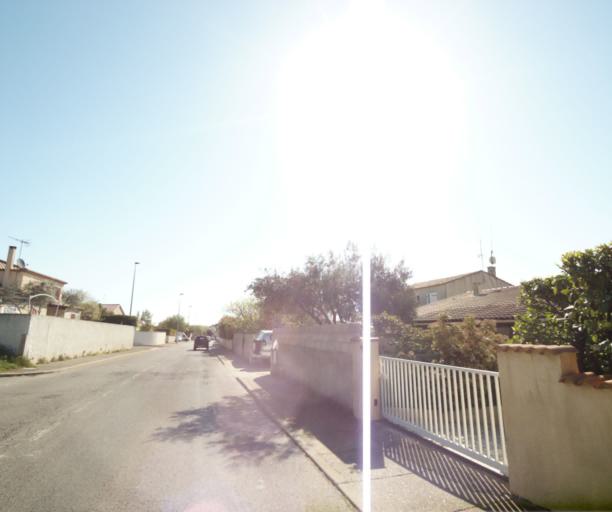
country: FR
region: Languedoc-Roussillon
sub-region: Departement de l'Herault
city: Castelnau-le-Lez
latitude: 43.6365
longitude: 3.9204
